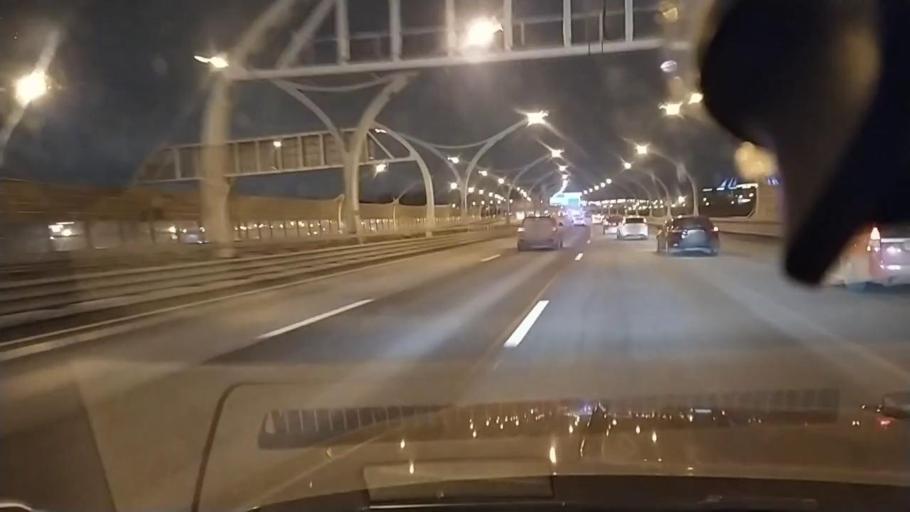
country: RU
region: St.-Petersburg
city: Staraya Derevnya
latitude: 59.9966
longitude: 30.2312
